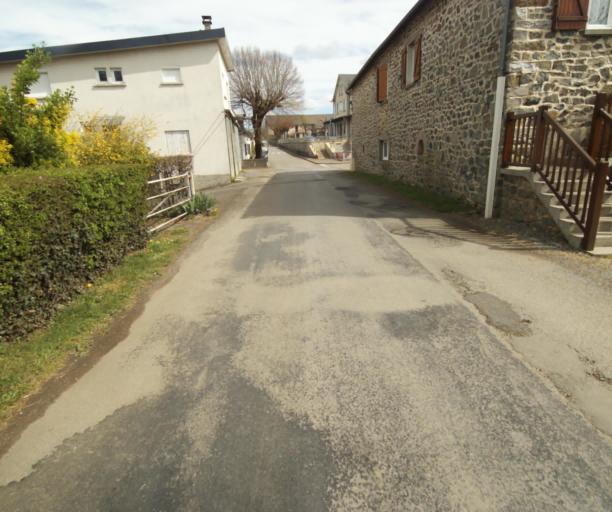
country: FR
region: Limousin
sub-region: Departement de la Correze
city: Laguenne
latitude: 45.2329
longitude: 1.8370
